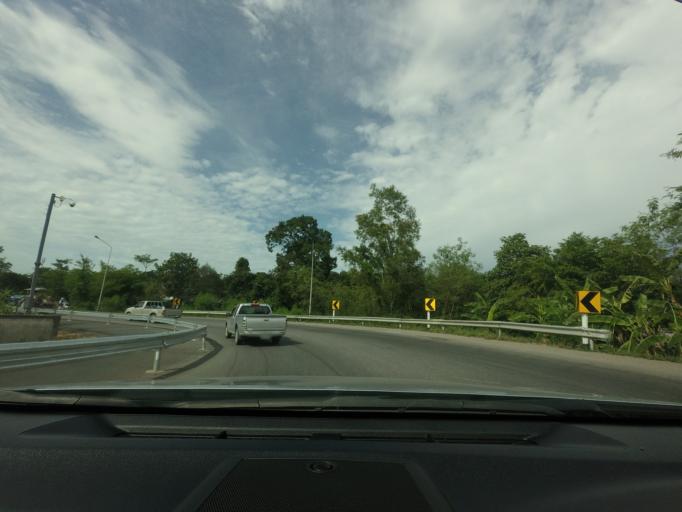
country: TH
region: Songkhla
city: Khlong Hoi Khong
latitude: 6.9239
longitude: 100.4167
